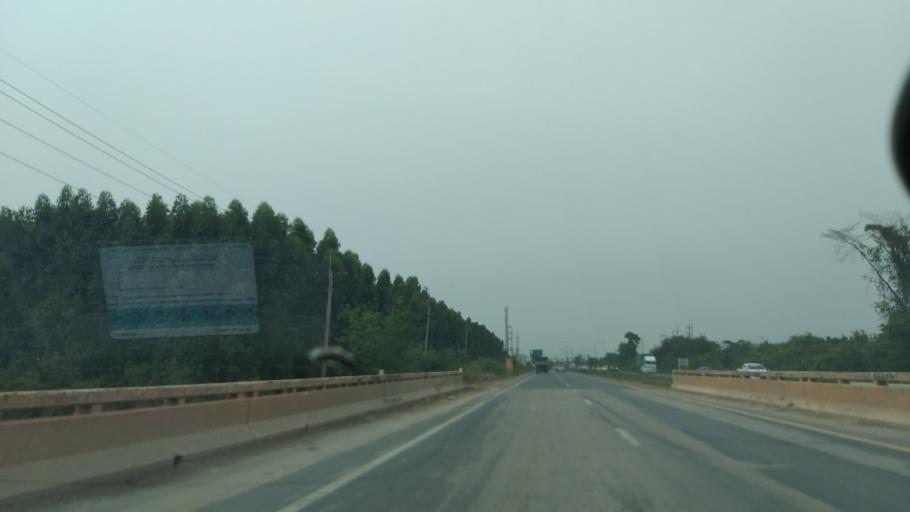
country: TH
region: Chachoengsao
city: Plaeng Yao
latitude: 13.5660
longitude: 101.2681
